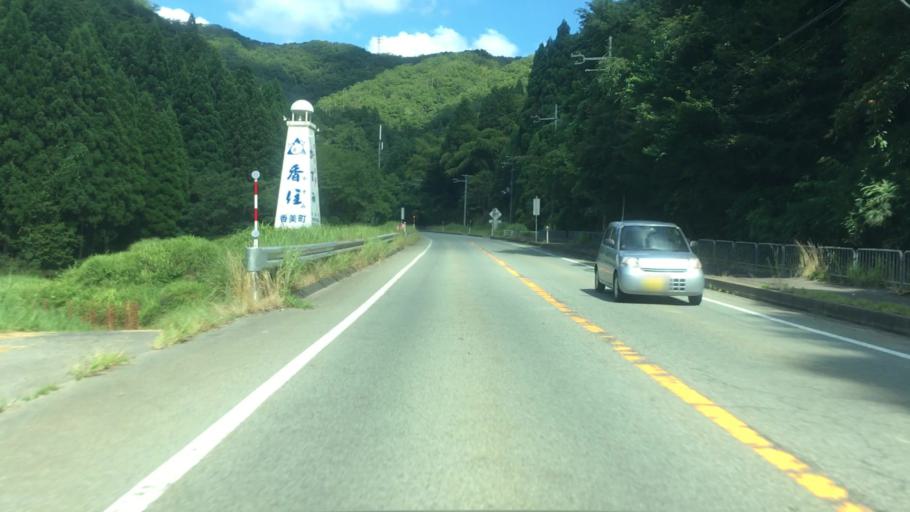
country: JP
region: Hyogo
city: Toyooka
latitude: 35.5770
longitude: 134.7537
